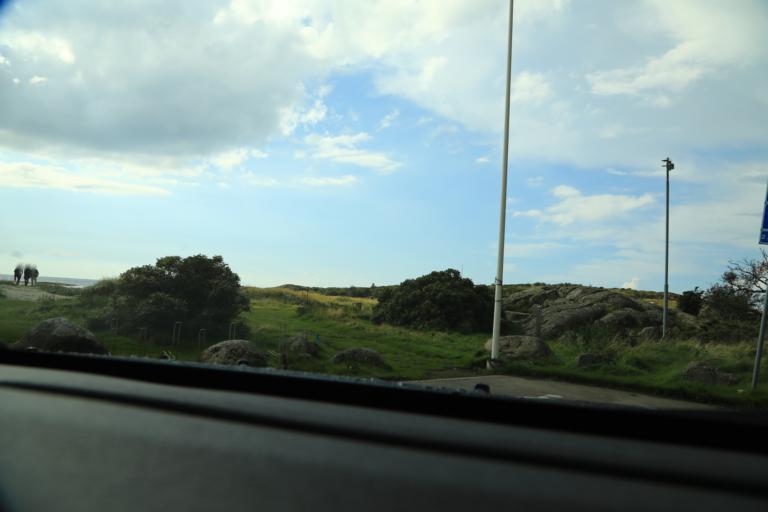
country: SE
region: Halland
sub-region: Varbergs Kommun
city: Varberg
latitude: 57.1187
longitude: 12.2037
